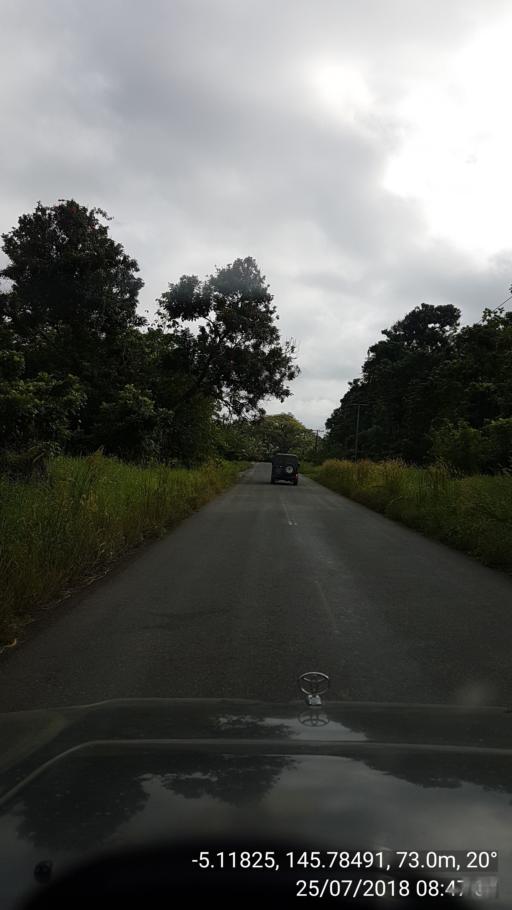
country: PG
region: Madang
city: Madang
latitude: -5.1183
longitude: 145.7850
